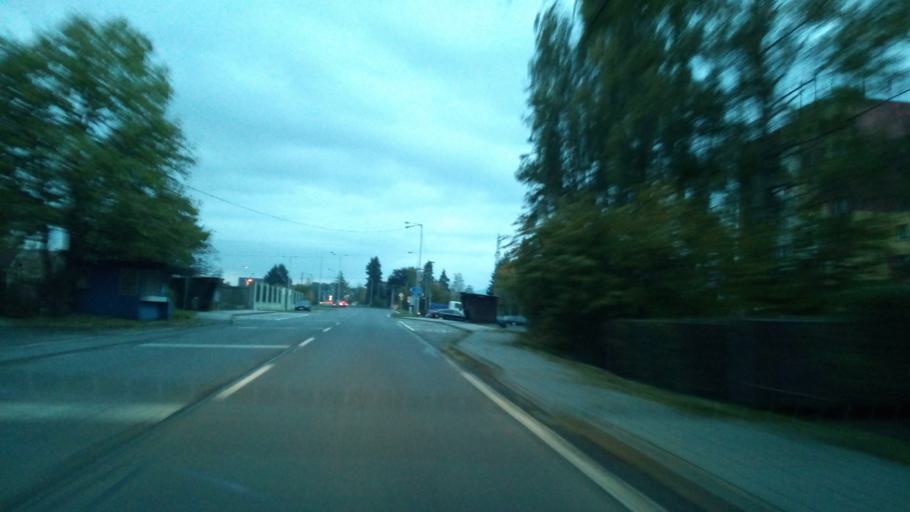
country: CZ
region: Moravskoslezsky
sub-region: Okres Frydek-Mistek
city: Stare Mesto
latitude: 49.6769
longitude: 18.3655
